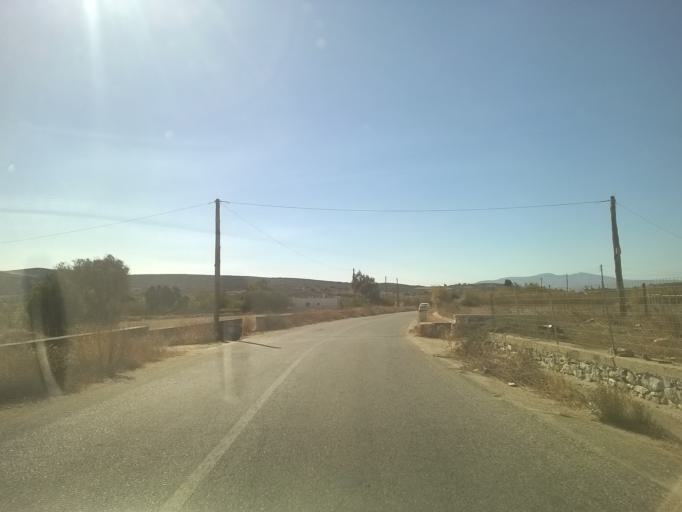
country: GR
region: South Aegean
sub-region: Nomos Kykladon
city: Filotion
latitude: 37.0433
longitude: 25.4245
